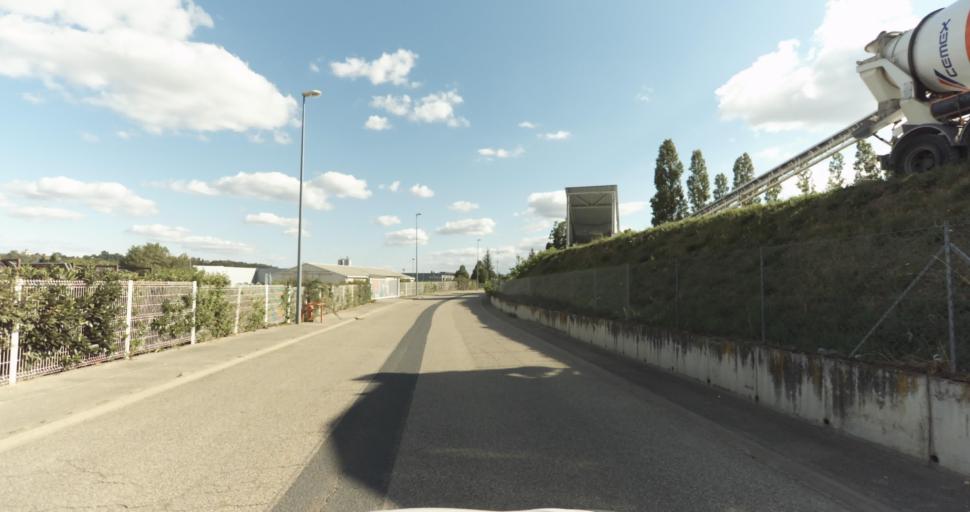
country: FR
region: Rhone-Alpes
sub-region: Departement du Rhone
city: Chaponost
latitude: 45.7040
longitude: 4.7652
